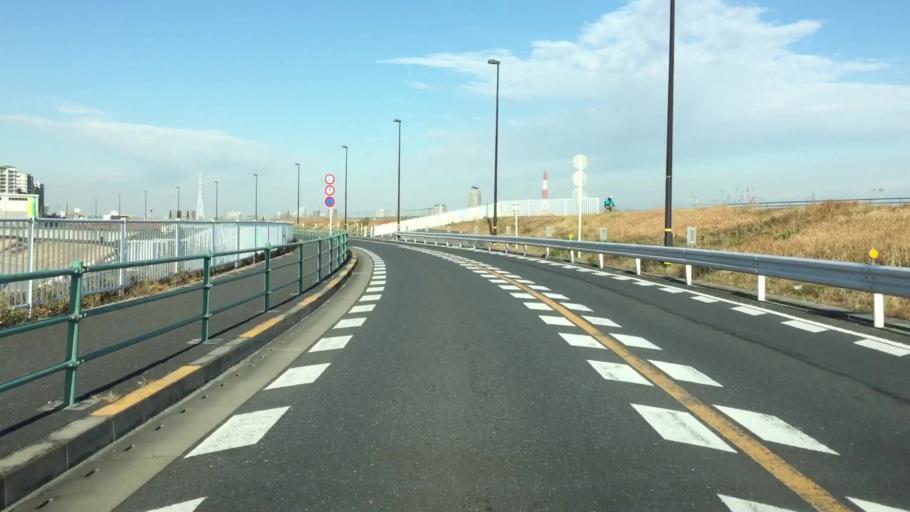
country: JP
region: Saitama
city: Kawaguchi
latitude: 35.7675
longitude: 139.7562
